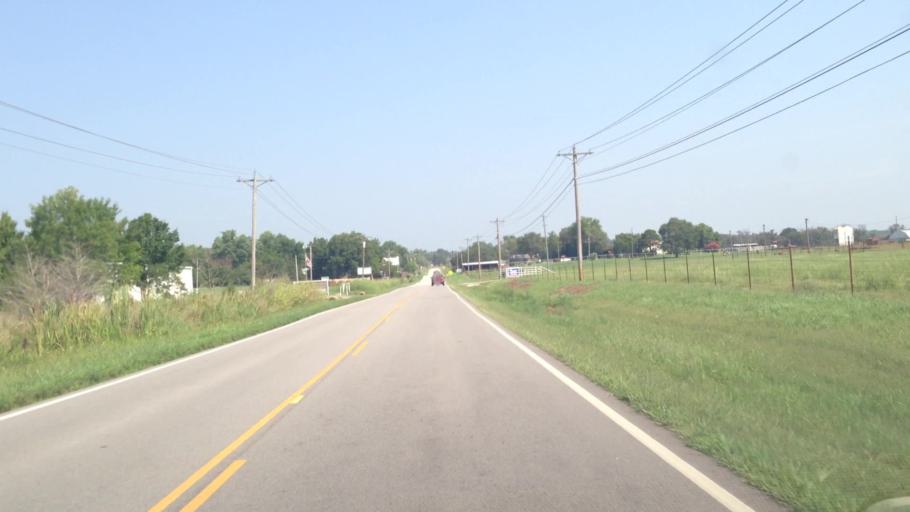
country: US
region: Oklahoma
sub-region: Delaware County
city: Cleora
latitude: 36.5742
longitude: -94.9707
